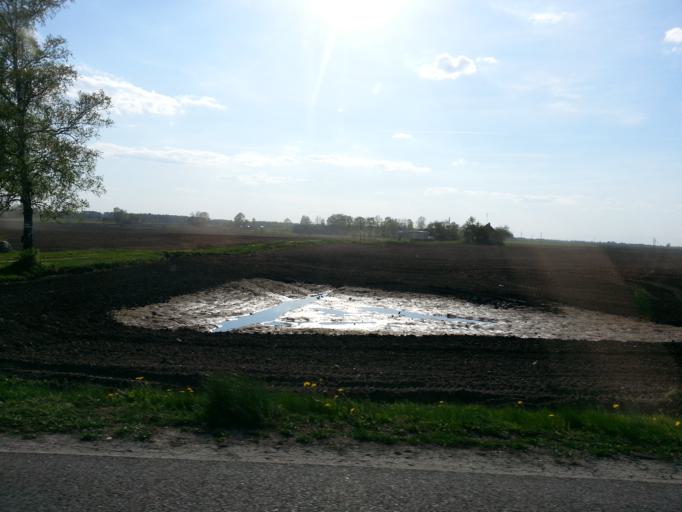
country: LT
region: Panevezys
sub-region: Panevezys City
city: Panevezys
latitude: 55.8881
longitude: 24.3419
